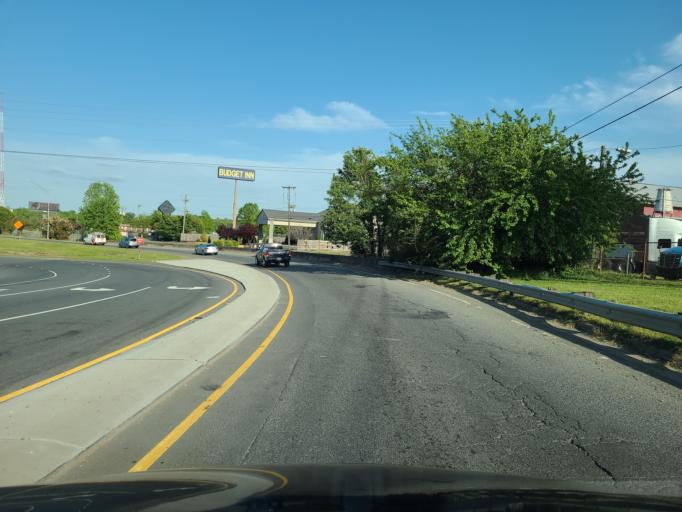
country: US
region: North Carolina
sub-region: Mecklenburg County
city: Charlotte
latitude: 35.2756
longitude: -80.8089
